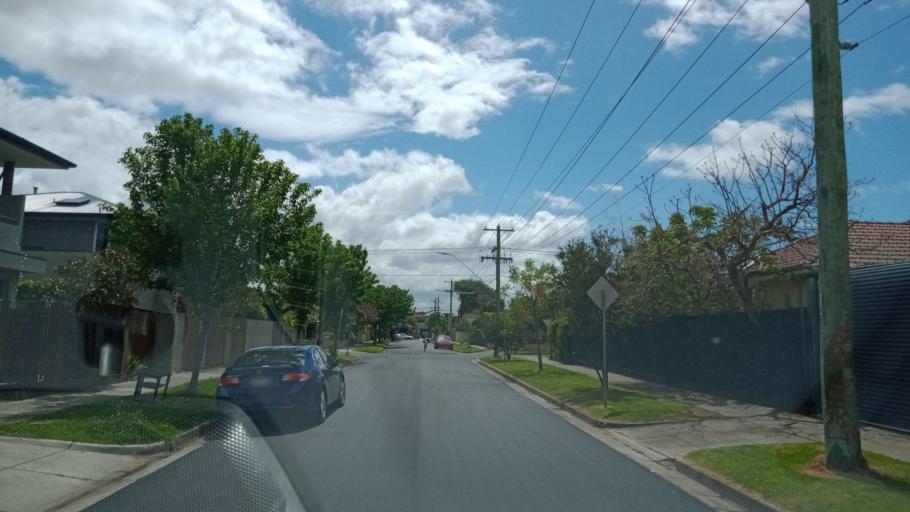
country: AU
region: Victoria
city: McKinnon
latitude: -37.9146
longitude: 145.0546
